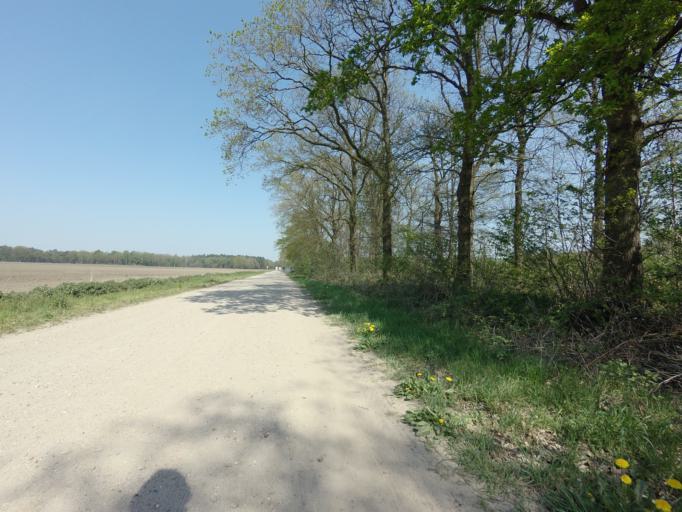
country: NL
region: North Brabant
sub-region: Gemeente Baarle-Nassau
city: Baarle-Nassau
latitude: 51.4920
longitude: 4.9906
